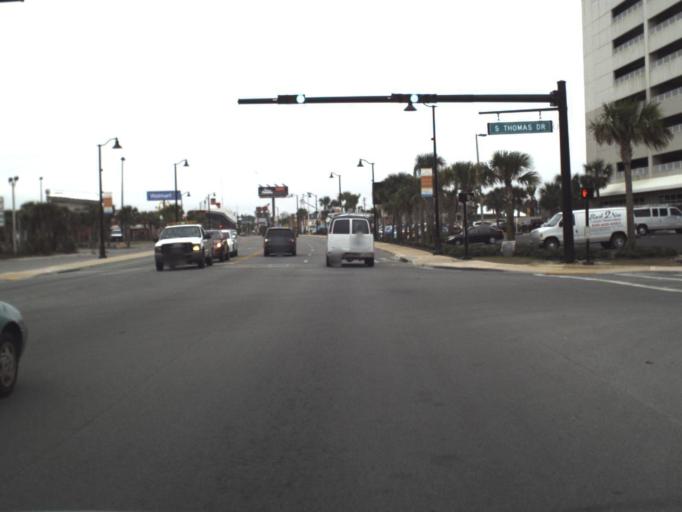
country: US
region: Florida
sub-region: Bay County
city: Panama City Beach
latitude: 30.1779
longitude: -85.8055
